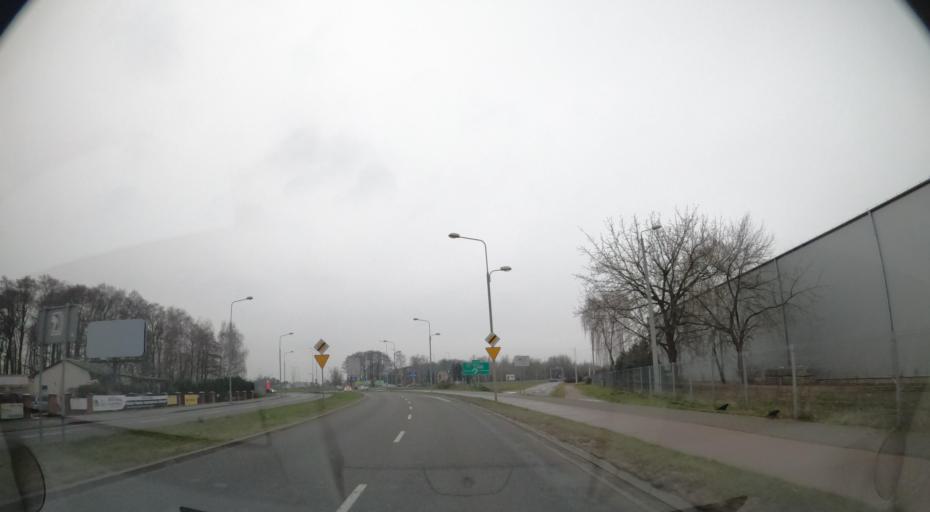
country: PL
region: Masovian Voivodeship
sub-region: Radom
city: Radom
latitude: 51.4157
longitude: 21.2035
